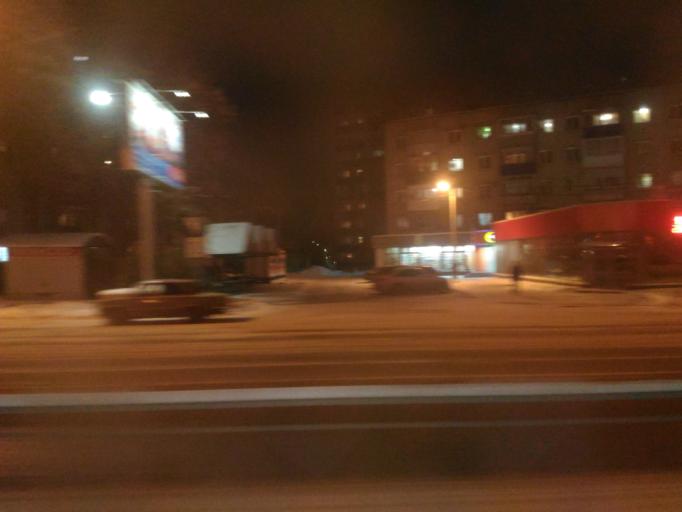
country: RU
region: Ulyanovsk
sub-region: Ulyanovskiy Rayon
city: Ulyanovsk
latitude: 54.3498
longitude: 48.3664
